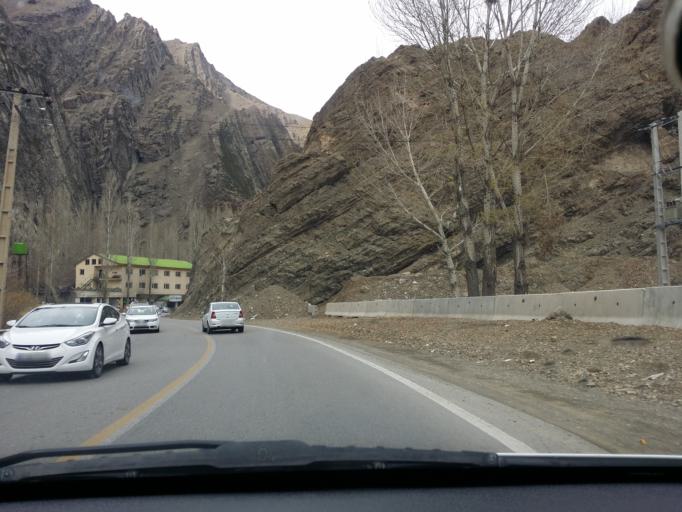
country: IR
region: Tehran
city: Tajrish
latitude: 36.0181
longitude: 51.2719
